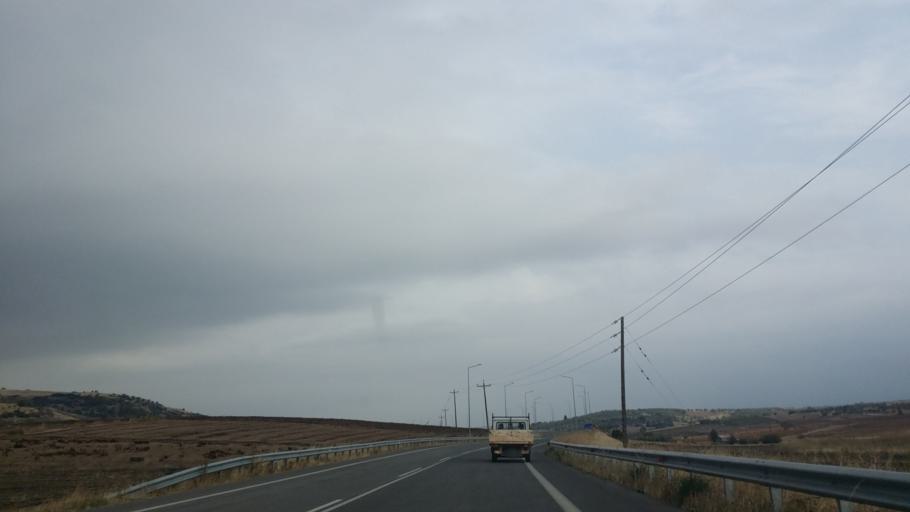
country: GR
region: Central Greece
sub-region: Nomos Voiotias
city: Thespies
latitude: 38.2970
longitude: 23.1627
